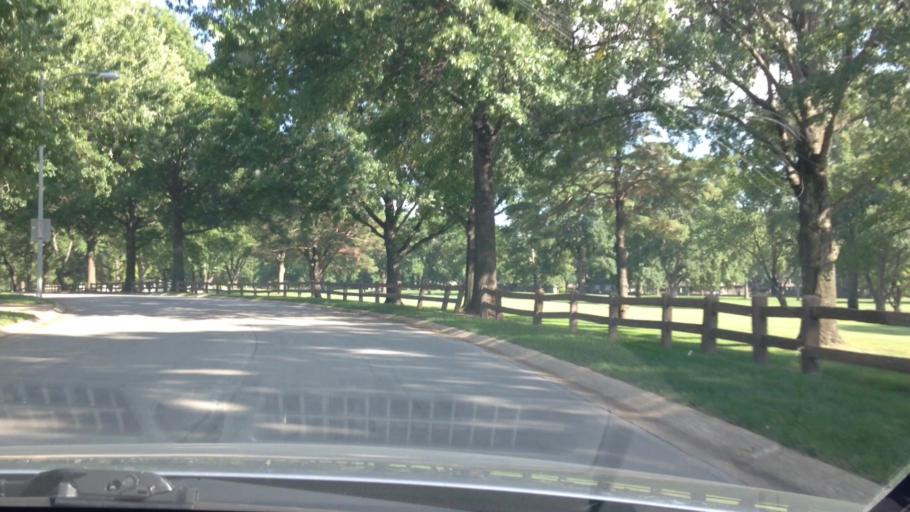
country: US
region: Kansas
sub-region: Johnson County
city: Leawood
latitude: 38.8980
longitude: -94.6212
